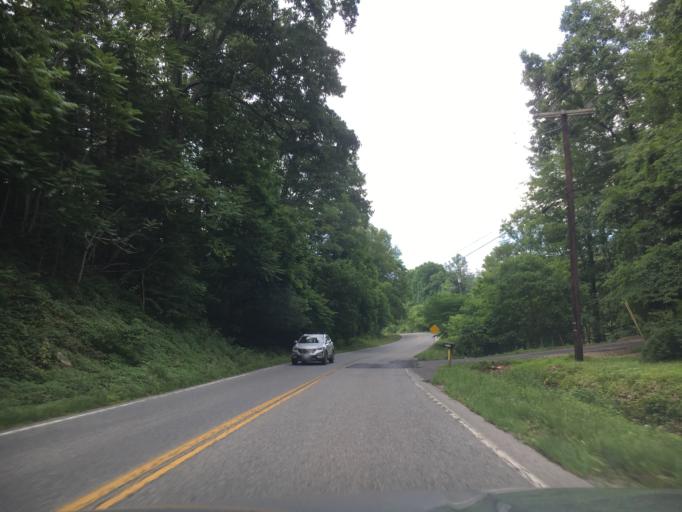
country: US
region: Virginia
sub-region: Roanoke County
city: Cave Spring
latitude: 37.1862
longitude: -80.0018
